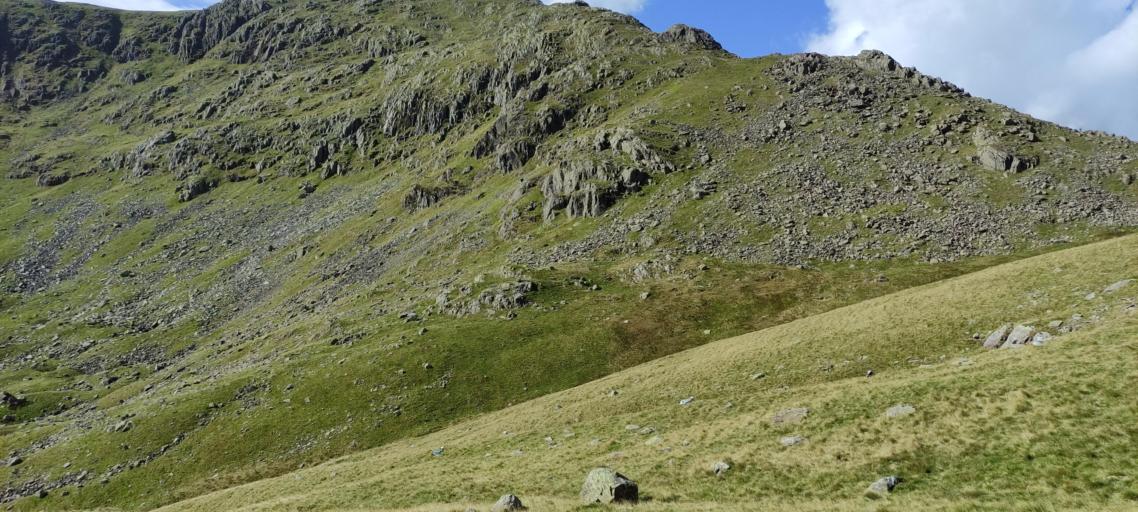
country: GB
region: England
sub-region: Cumbria
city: Ambleside
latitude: 54.3954
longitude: -3.1099
